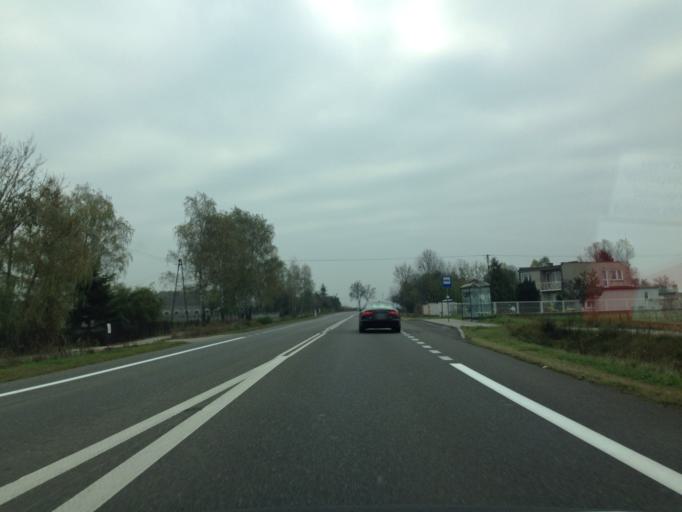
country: PL
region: Masovian Voivodeship
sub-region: Powiat plocki
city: Drobin
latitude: 52.7213
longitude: 20.0162
